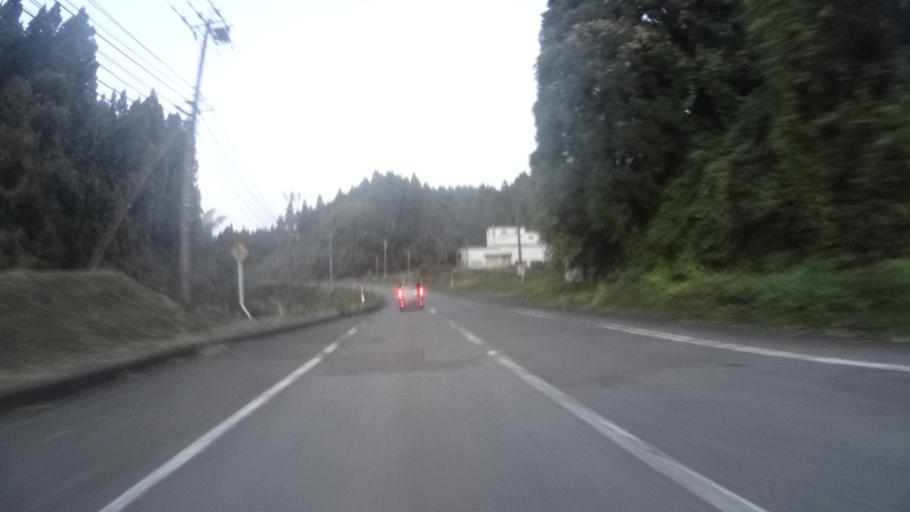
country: JP
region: Ishikawa
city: Nanao
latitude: 37.3499
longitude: 136.8628
